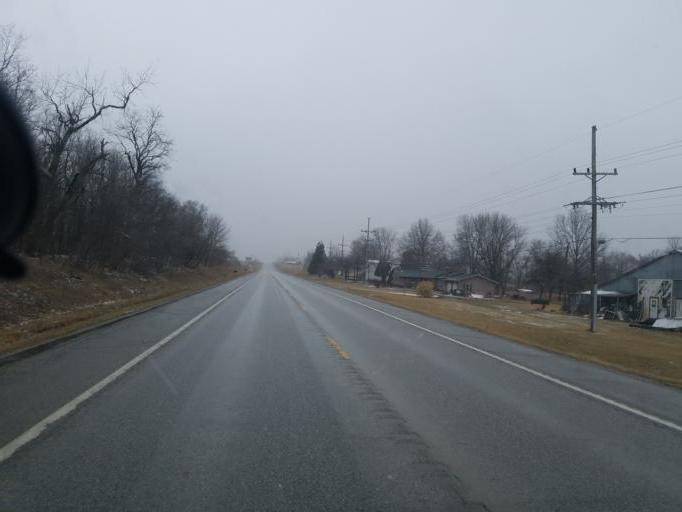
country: US
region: Missouri
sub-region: Adair County
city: Kirksville
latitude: 40.2668
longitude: -92.5825
